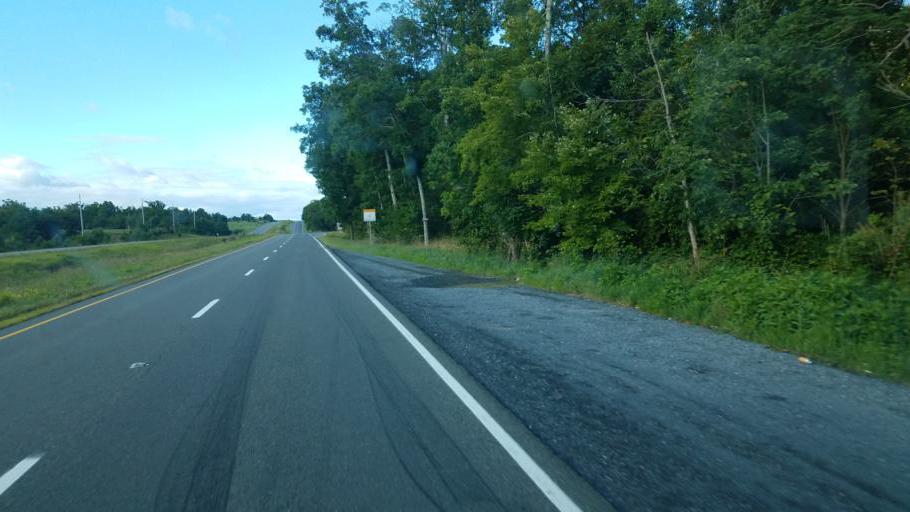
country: US
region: West Virginia
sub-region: Morgan County
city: Berkeley Springs
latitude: 39.4371
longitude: -78.3090
